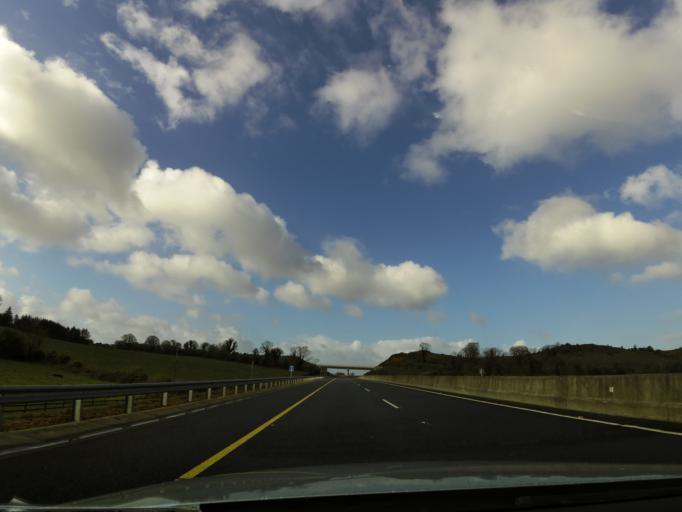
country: IE
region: Munster
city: Ballina
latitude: 52.7734
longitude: -8.3819
